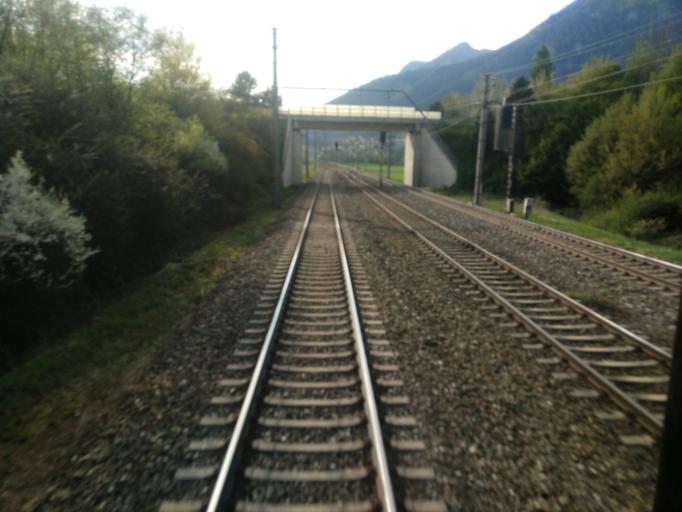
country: AT
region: Styria
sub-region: Politischer Bezirk Leoben
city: Kammern im Liesingtal
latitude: 47.3916
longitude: 14.9288
